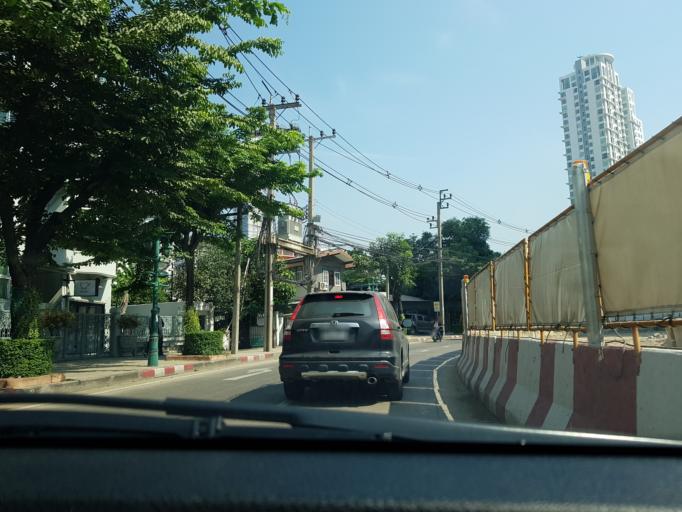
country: TH
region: Bangkok
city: Khlong San
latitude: 13.7218
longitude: 100.5061
